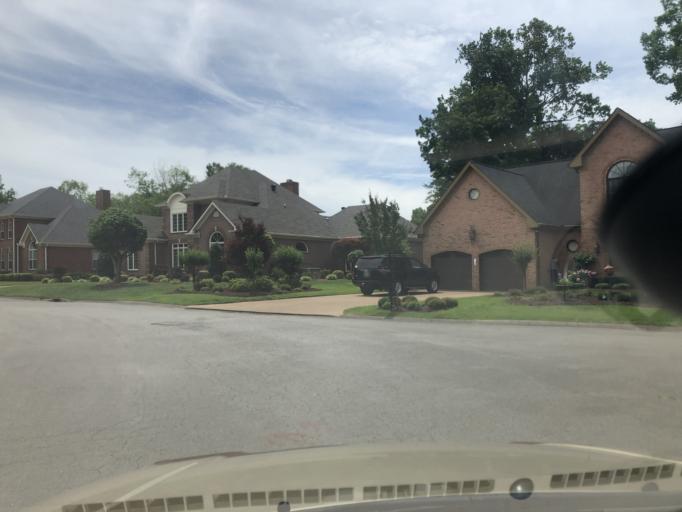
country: US
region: Tennessee
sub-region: Davidson County
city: Lakewood
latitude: 36.2597
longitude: -86.5866
